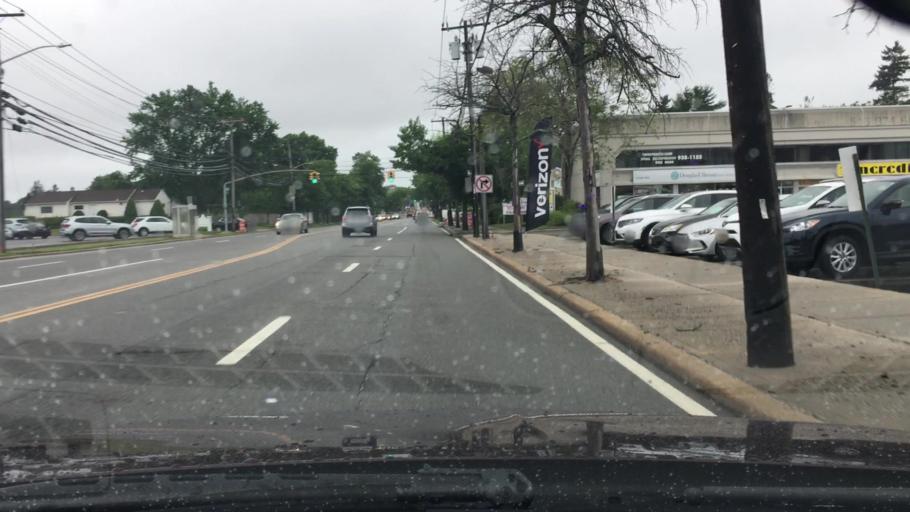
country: US
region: New York
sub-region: Nassau County
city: Plainview
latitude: 40.7757
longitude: -73.4732
